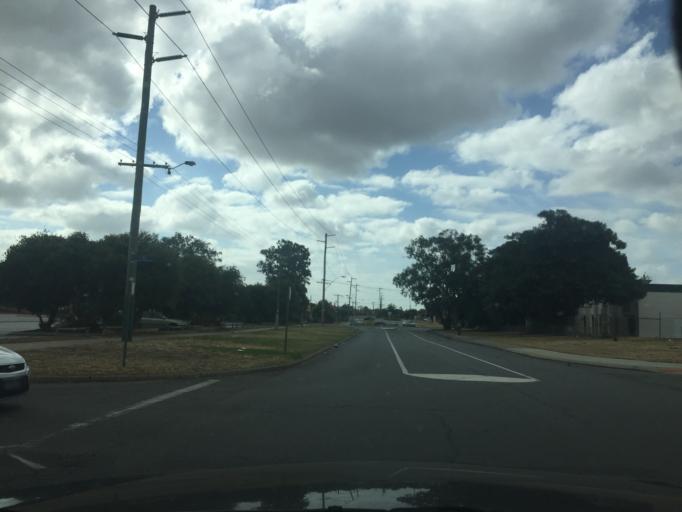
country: AU
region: Western Australia
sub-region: Gosnells
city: Maddington
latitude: -32.0515
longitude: 115.9786
